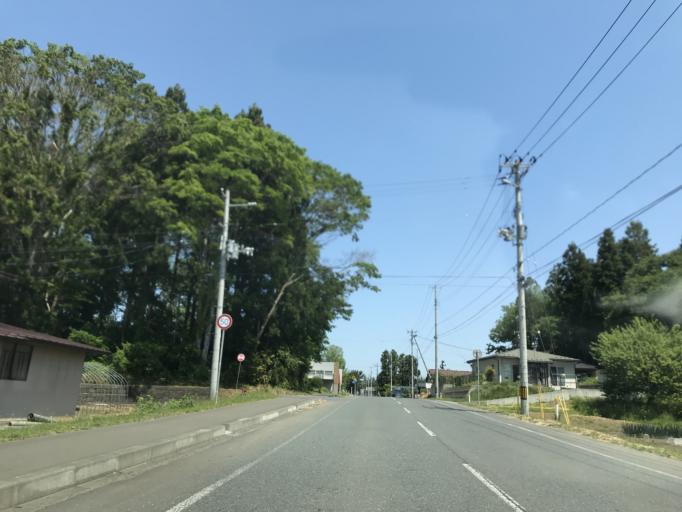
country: JP
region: Iwate
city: Kitakami
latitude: 39.2402
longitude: 141.0667
